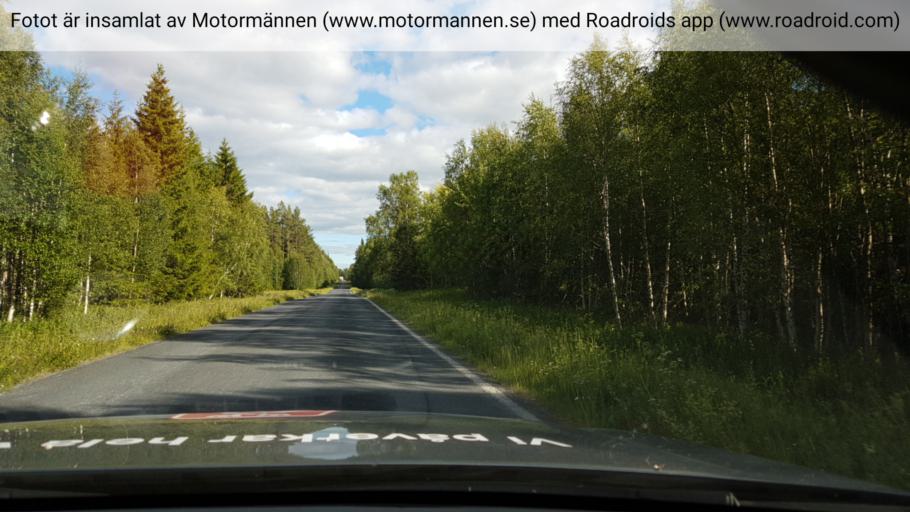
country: SE
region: Jaemtland
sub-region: Krokoms Kommun
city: Valla
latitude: 63.2824
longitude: 13.8940
